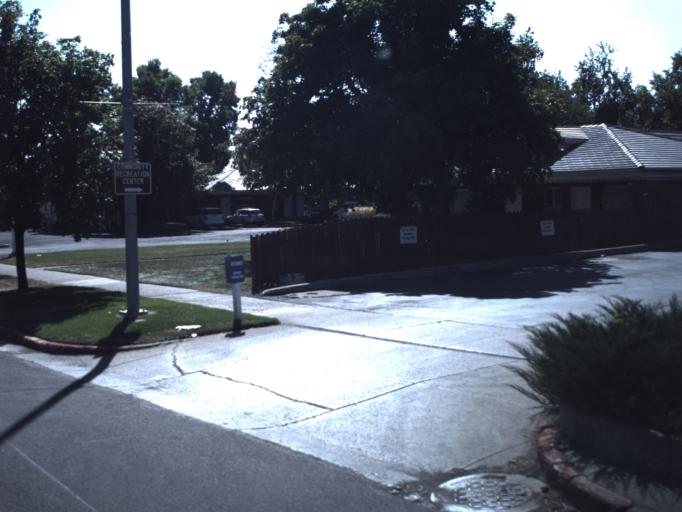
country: US
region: Utah
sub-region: Cache County
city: Logan
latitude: 41.7291
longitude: -111.8352
